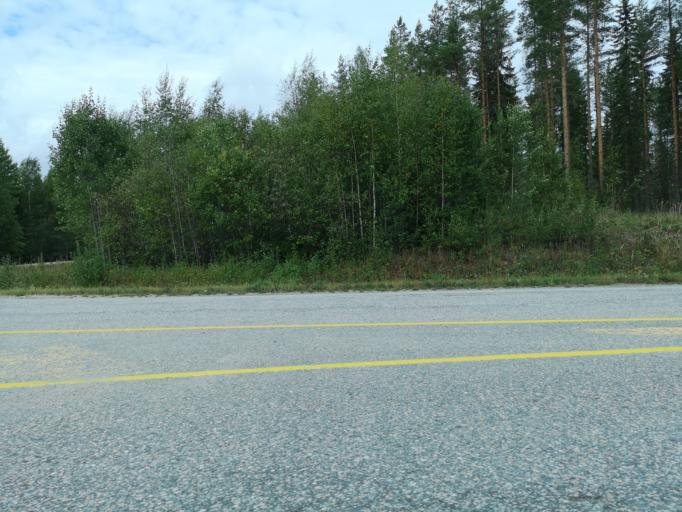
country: FI
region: Central Finland
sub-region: Jyvaeskylae
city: Hankasalmi
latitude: 62.3518
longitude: 26.4599
